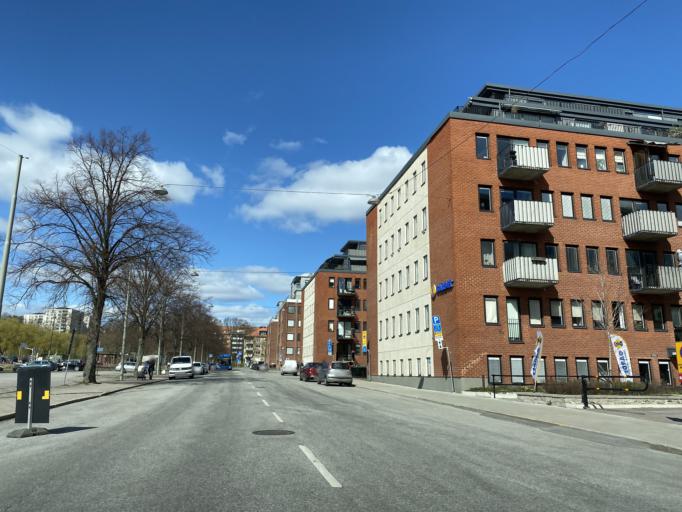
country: SE
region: Stockholm
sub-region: Stockholms Kommun
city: OEstermalm
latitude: 59.3411
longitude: 18.1111
